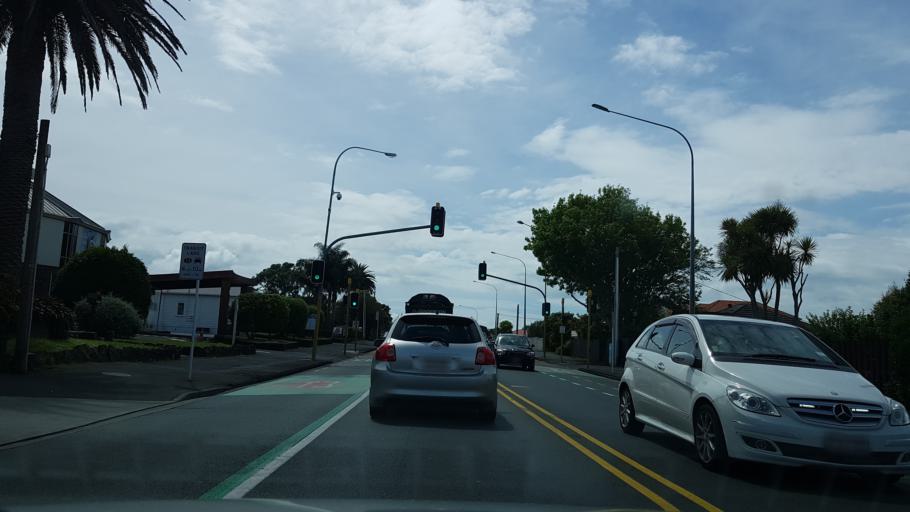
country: NZ
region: Auckland
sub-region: Auckland
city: North Shore
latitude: -36.8105
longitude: 174.7379
